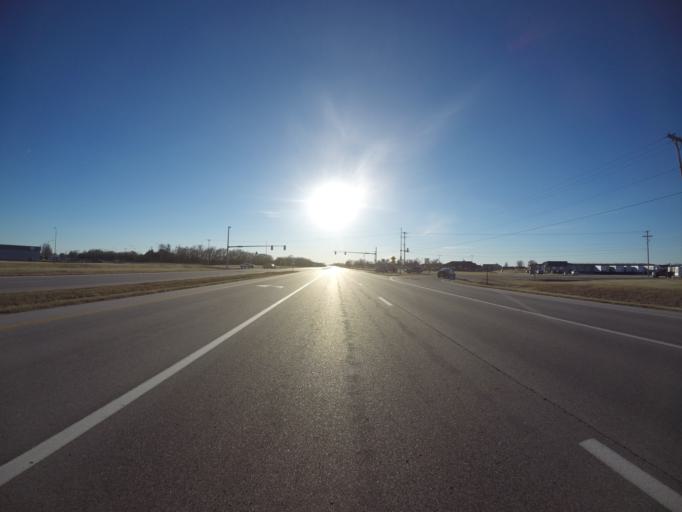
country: US
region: Kansas
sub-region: Sedgwick County
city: Goddard
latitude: 37.6262
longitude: -97.4605
